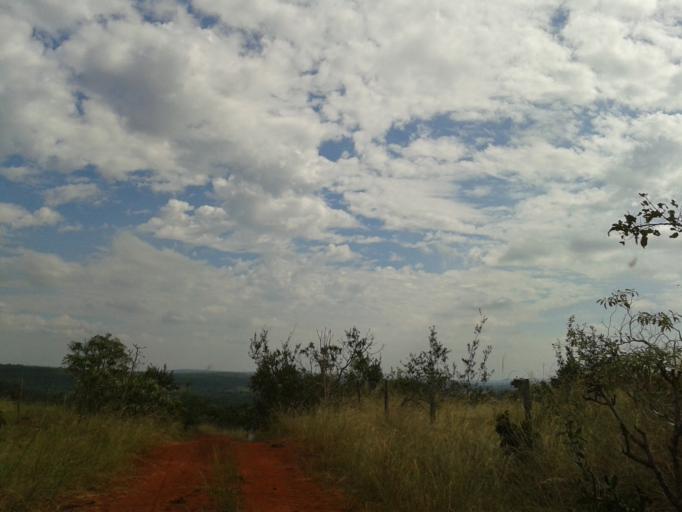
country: BR
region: Minas Gerais
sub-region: Campina Verde
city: Campina Verde
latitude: -19.3924
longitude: -49.6590
